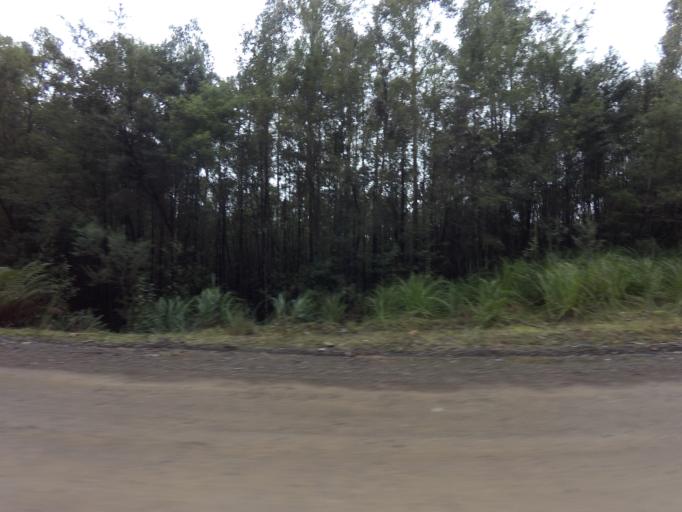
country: AU
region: Tasmania
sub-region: Huon Valley
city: Geeveston
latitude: -43.4780
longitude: 146.8909
